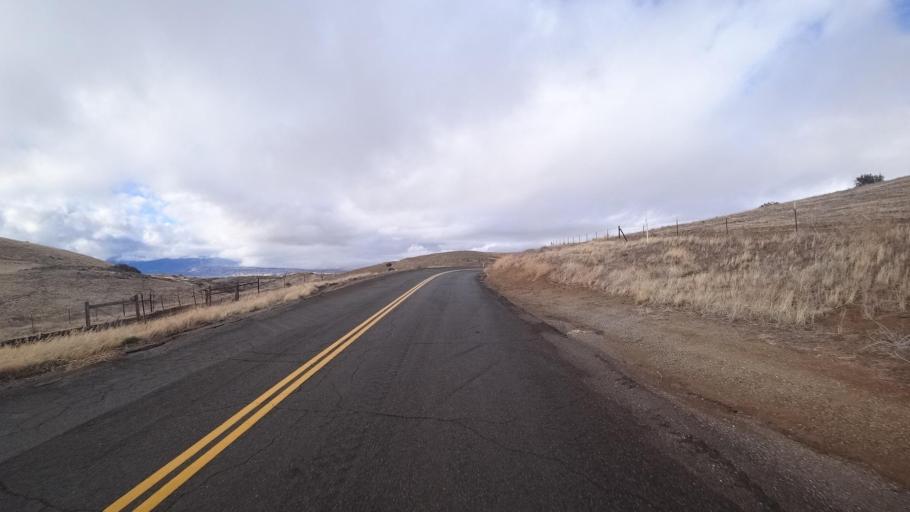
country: US
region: California
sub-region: Kern County
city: Maricopa
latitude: 34.9163
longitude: -119.4061
